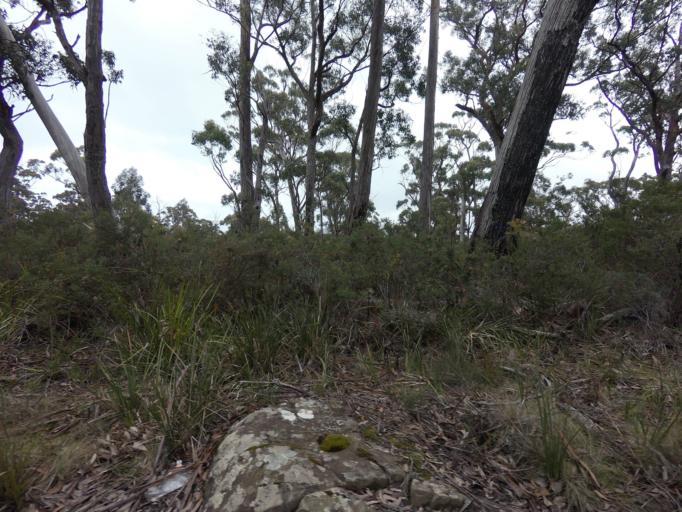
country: AU
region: Tasmania
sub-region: Huon Valley
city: Geeveston
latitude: -43.4695
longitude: 146.9322
